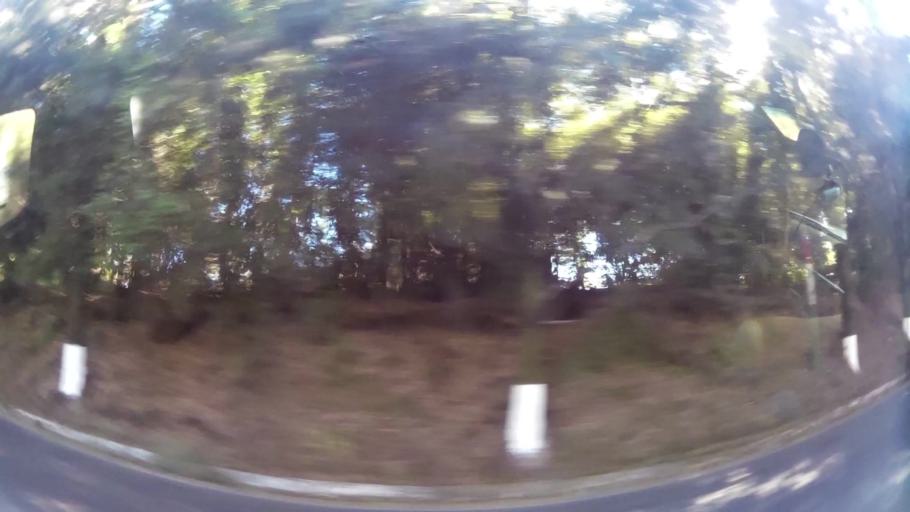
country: GT
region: Guatemala
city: Fraijanes
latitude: 14.4757
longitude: -90.4517
